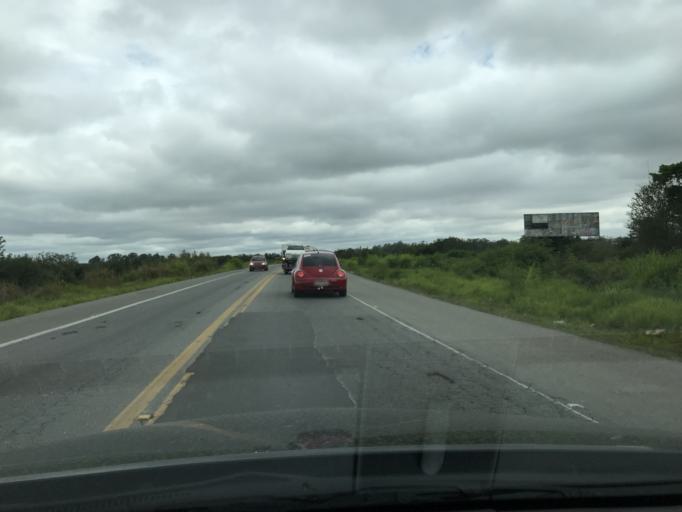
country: BR
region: Sao Paulo
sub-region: Itaquaquecetuba
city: Itaquaquecetuba
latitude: -23.4803
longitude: -46.3261
